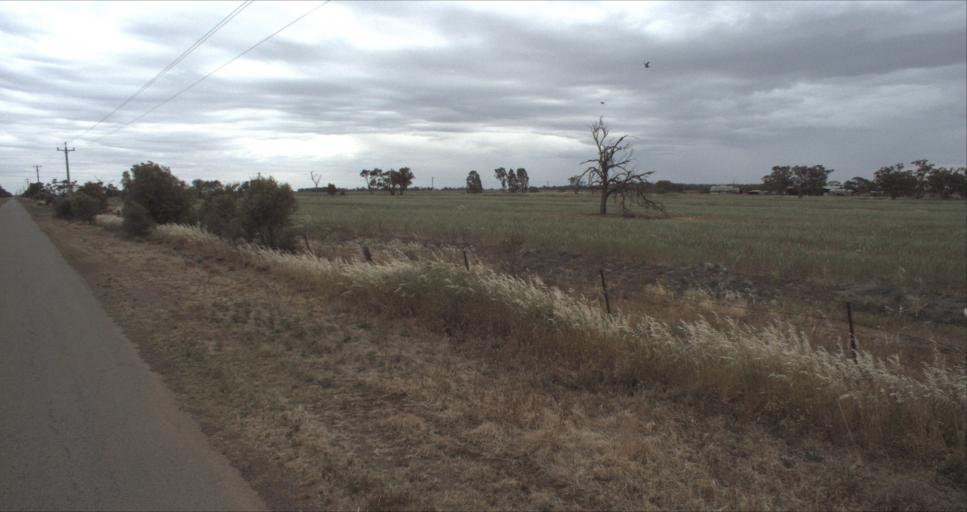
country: AU
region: New South Wales
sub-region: Leeton
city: Leeton
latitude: -34.4126
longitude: 146.3400
